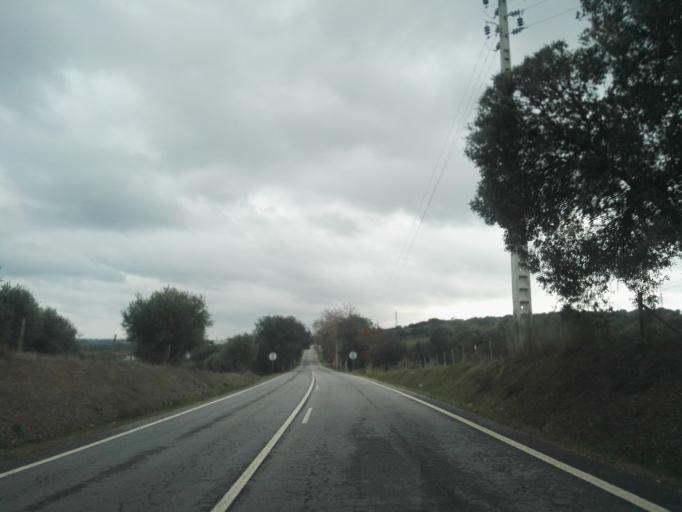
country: PT
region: Portalegre
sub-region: Arronches
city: Arronches
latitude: 39.1184
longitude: -7.2933
